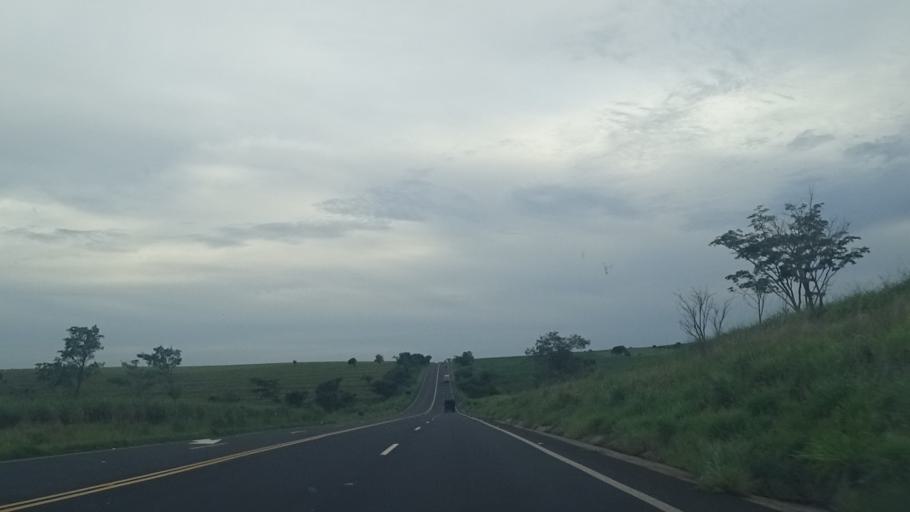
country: BR
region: Sao Paulo
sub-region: Martinopolis
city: Martinopolis
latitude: -22.0703
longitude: -51.1052
